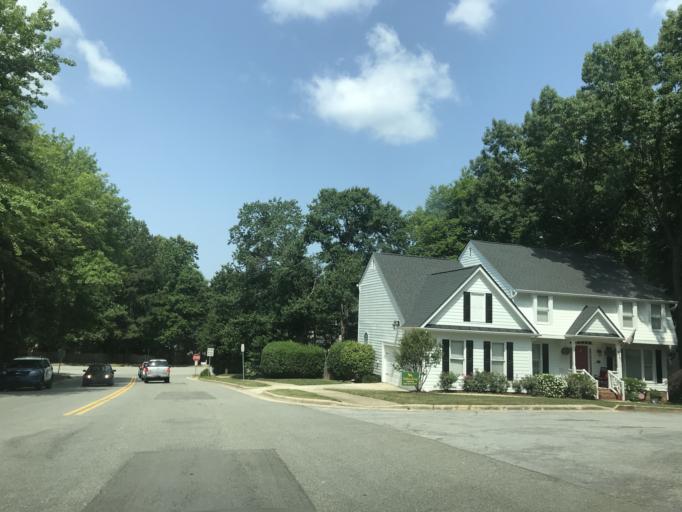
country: US
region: North Carolina
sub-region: Wake County
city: West Raleigh
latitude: 35.8974
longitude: -78.6618
